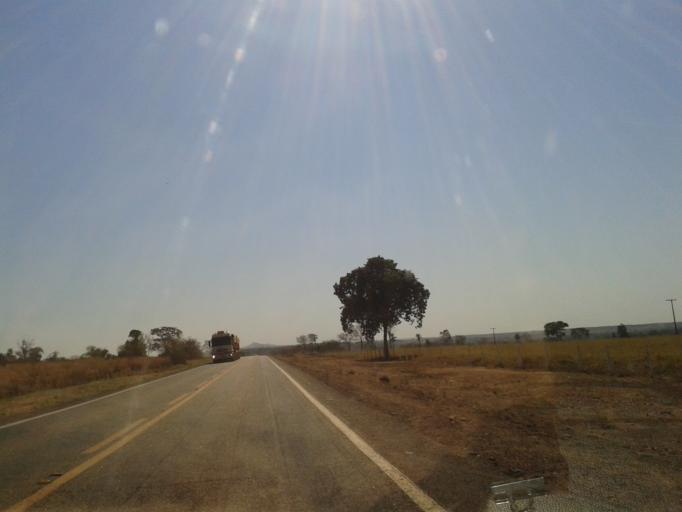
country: BR
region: Goias
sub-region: Crixas
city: Crixas
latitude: -14.1963
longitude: -50.3856
